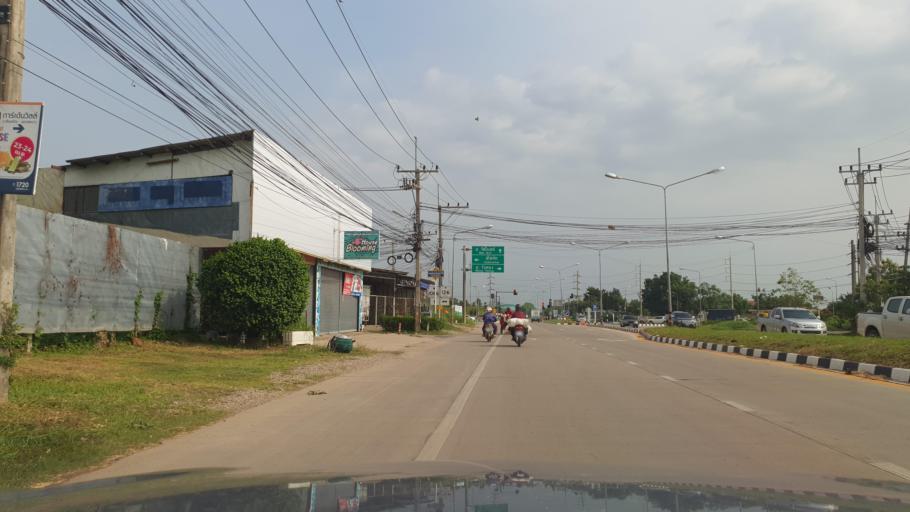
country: TH
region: Phitsanulok
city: Phitsanulok
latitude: 16.8632
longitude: 100.2502
